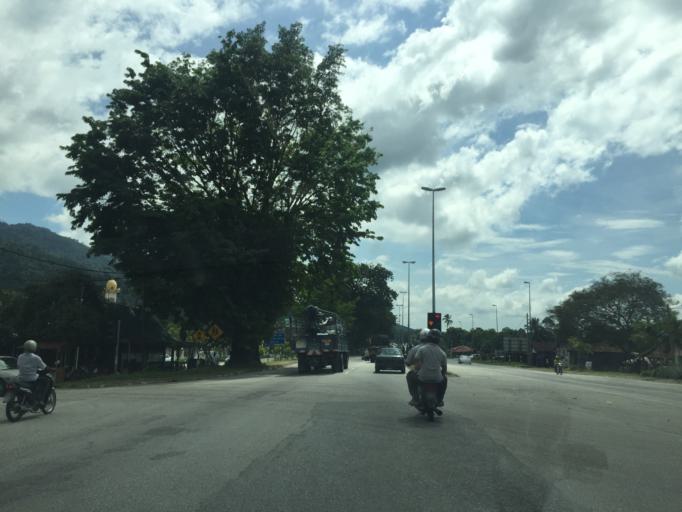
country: MY
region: Perak
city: Kampar
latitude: 4.3053
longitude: 101.1561
